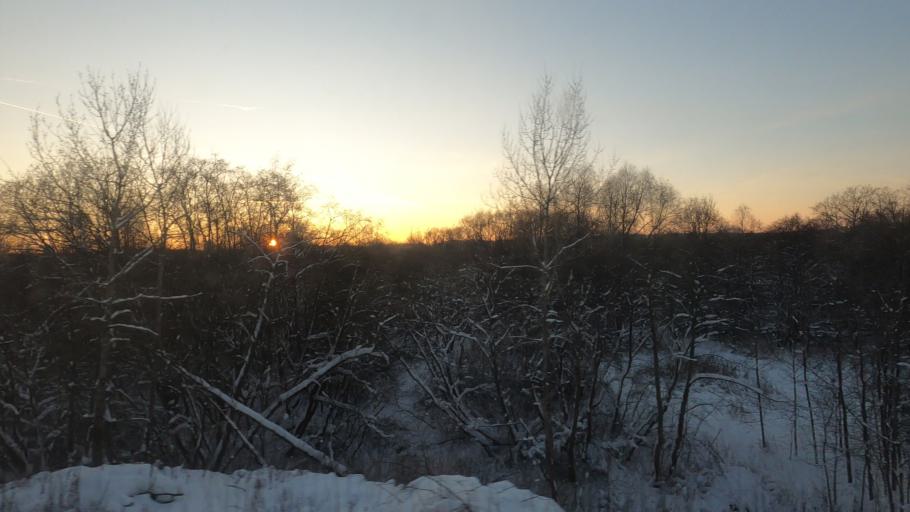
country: RU
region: Moskovskaya
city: Dedenevo
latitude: 56.2673
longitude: 37.5095
